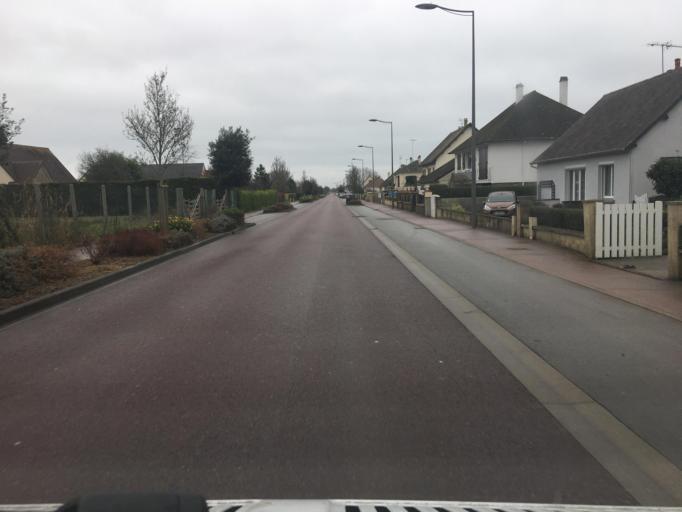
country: FR
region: Lower Normandy
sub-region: Departement de la Manche
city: Quettehou
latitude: 49.5911
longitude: -1.2935
